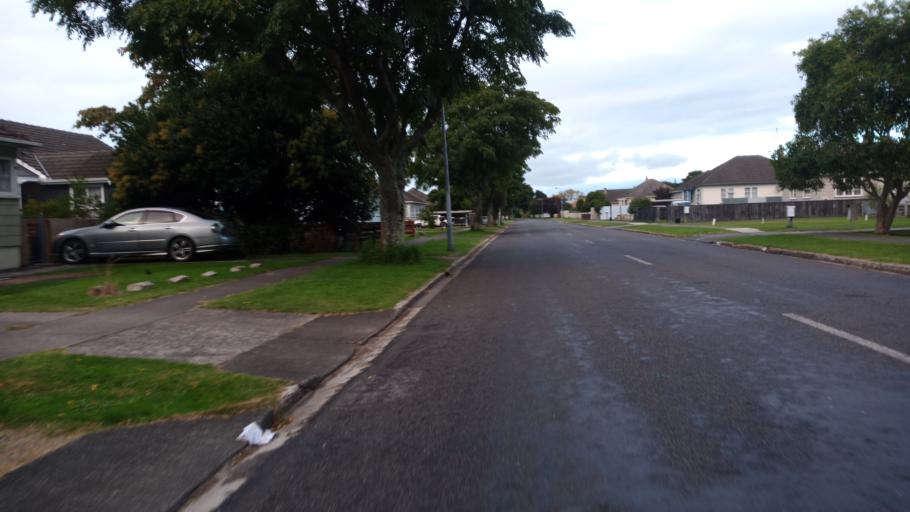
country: NZ
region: Gisborne
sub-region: Gisborne District
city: Gisborne
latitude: -38.6546
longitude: 178.0047
